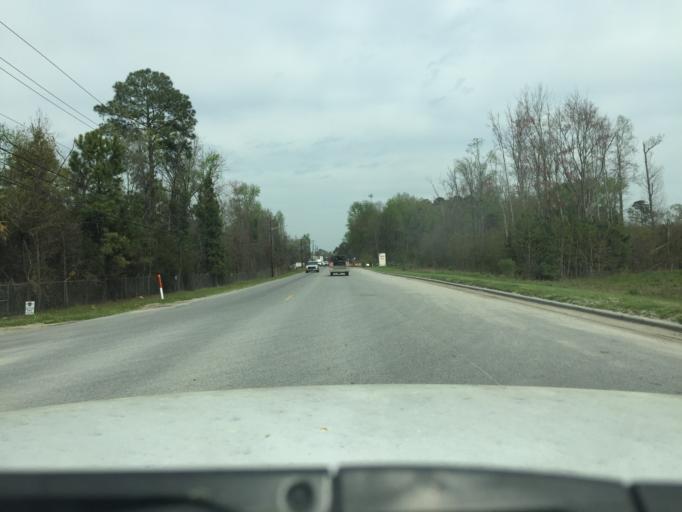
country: US
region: Georgia
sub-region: Chatham County
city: Garden City
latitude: 32.0812
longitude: -81.1418
